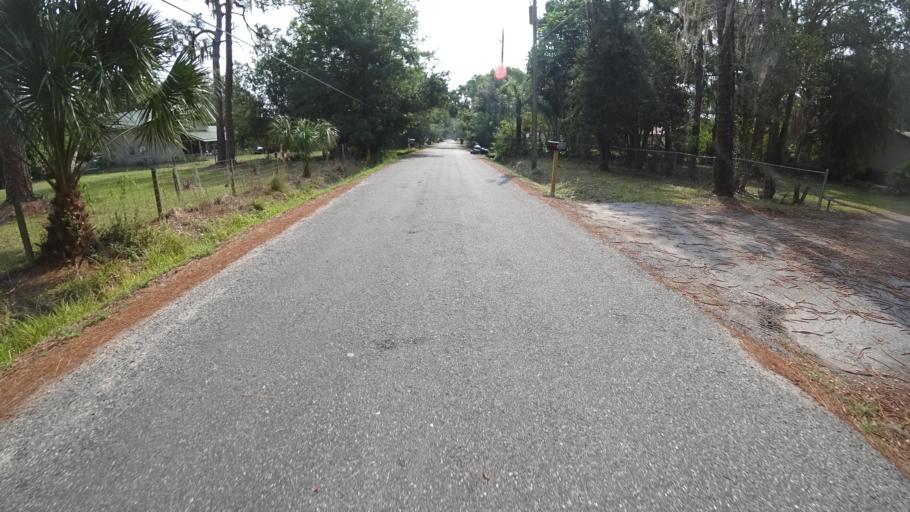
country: US
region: Florida
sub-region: Manatee County
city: Samoset
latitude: 27.4731
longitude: -82.5040
